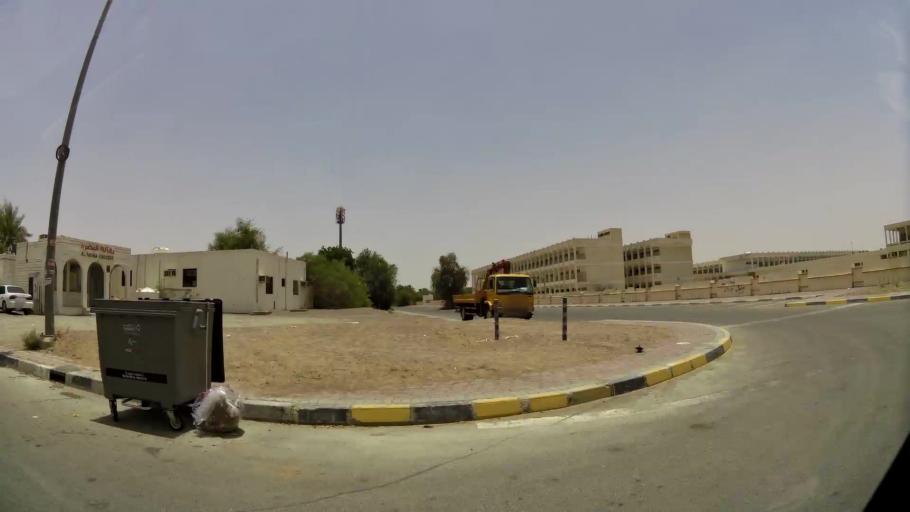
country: AE
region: Abu Dhabi
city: Al Ain
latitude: 24.2183
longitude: 55.7160
